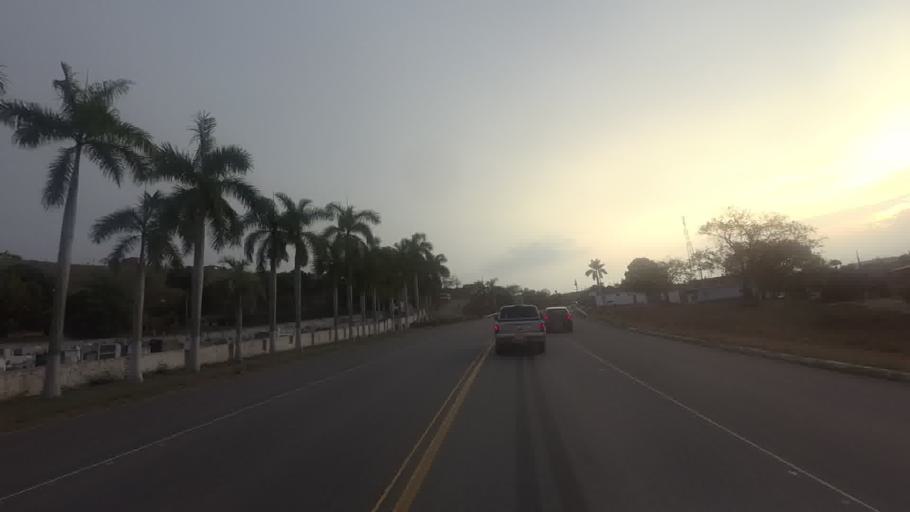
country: BR
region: Rio de Janeiro
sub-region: Carmo
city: Carmo
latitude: -21.7738
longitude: -42.5331
